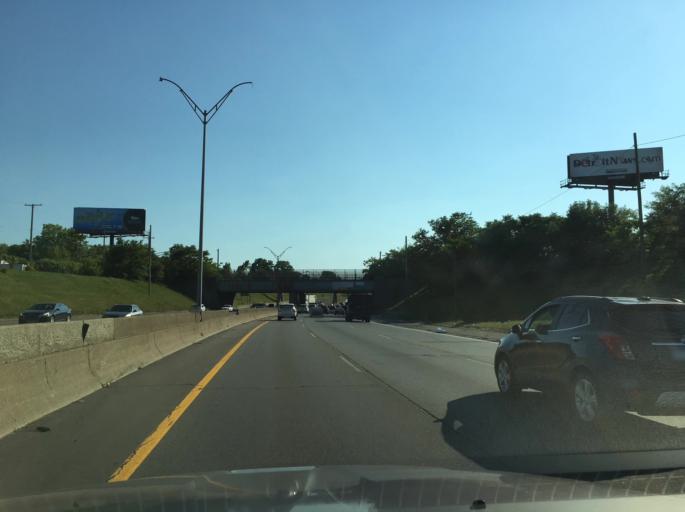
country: US
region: Michigan
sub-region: Wayne County
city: Grosse Pointe Park
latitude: 42.3946
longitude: -82.9904
